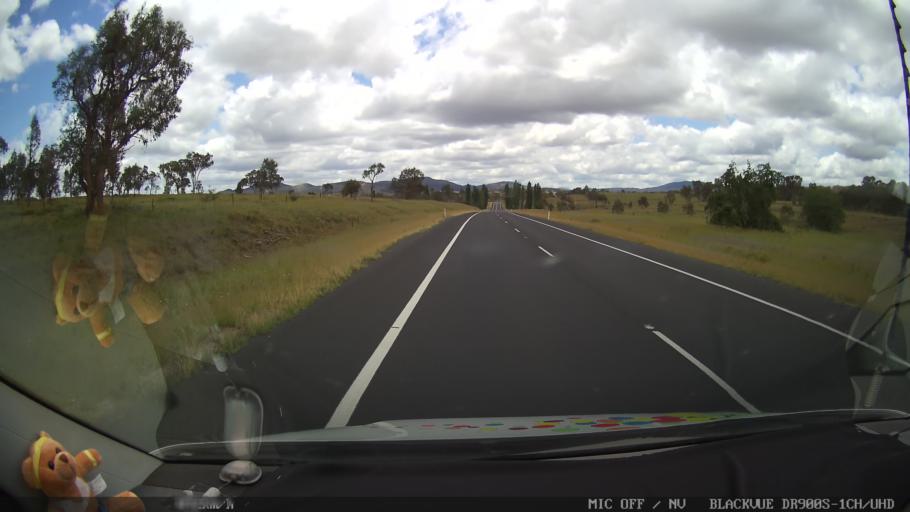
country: AU
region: New South Wales
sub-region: Glen Innes Severn
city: Glen Innes
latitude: -29.3916
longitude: 151.8832
